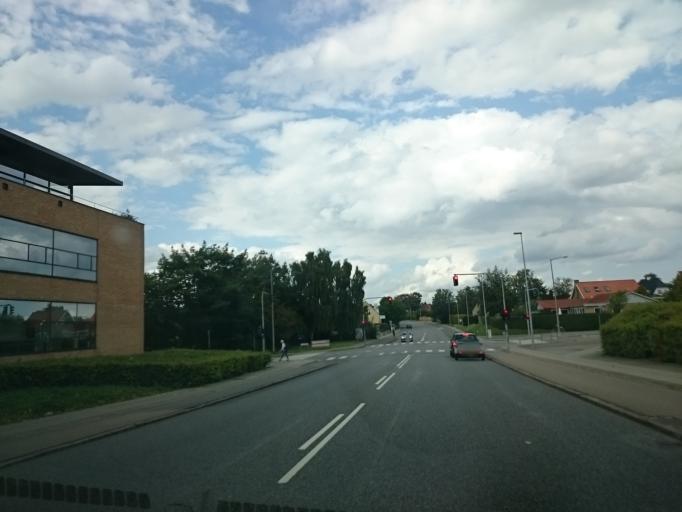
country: DK
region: Central Jutland
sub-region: Arhus Kommune
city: Arhus
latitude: 56.1299
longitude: 10.1738
